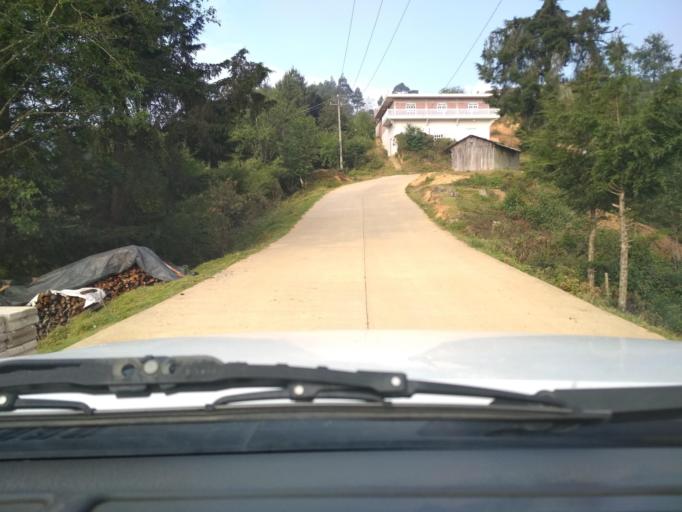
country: MX
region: Veracruz
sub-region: Soledad Atzompa
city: Tlatilpa
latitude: 18.7490
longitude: -97.1520
